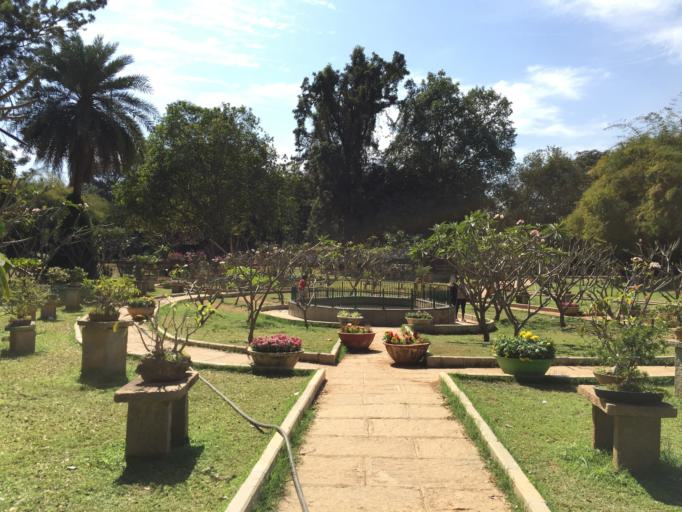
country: IN
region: Karnataka
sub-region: Bangalore Urban
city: Bangalore
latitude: 12.9502
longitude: 77.5897
